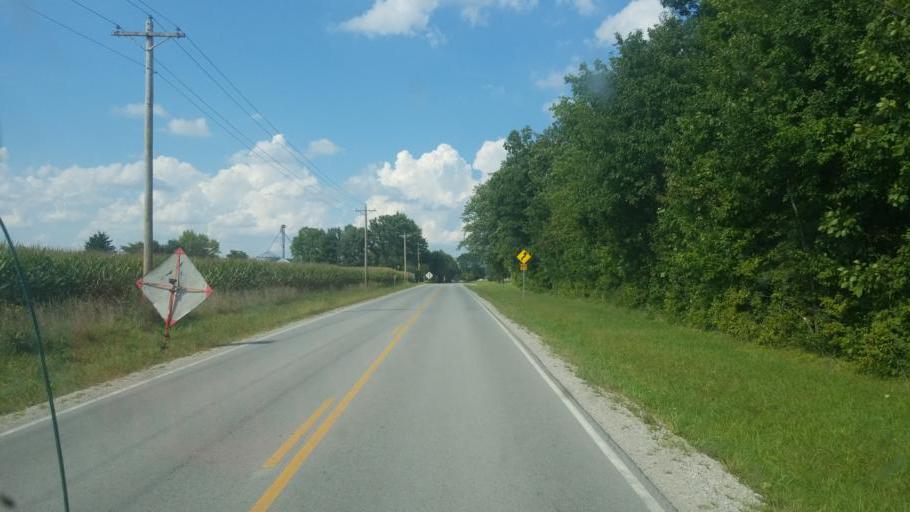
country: US
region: Ohio
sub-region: Huron County
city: Willard
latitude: 40.9951
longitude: -82.8532
